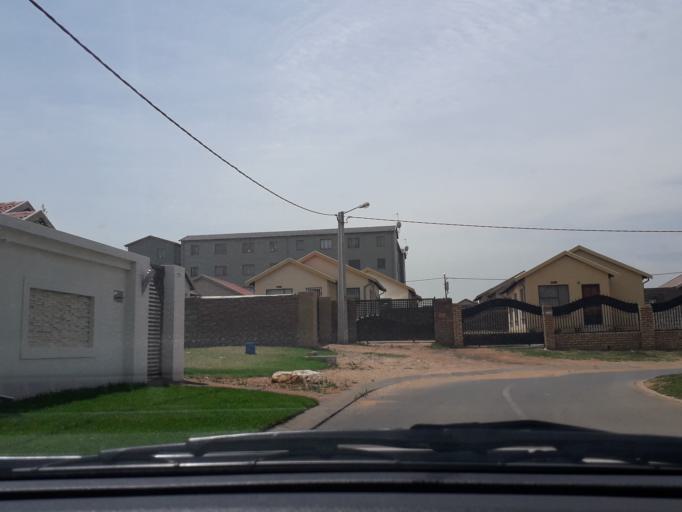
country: ZA
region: Gauteng
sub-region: City of Johannesburg Metropolitan Municipality
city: Roodepoort
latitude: -26.2048
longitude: 27.9111
